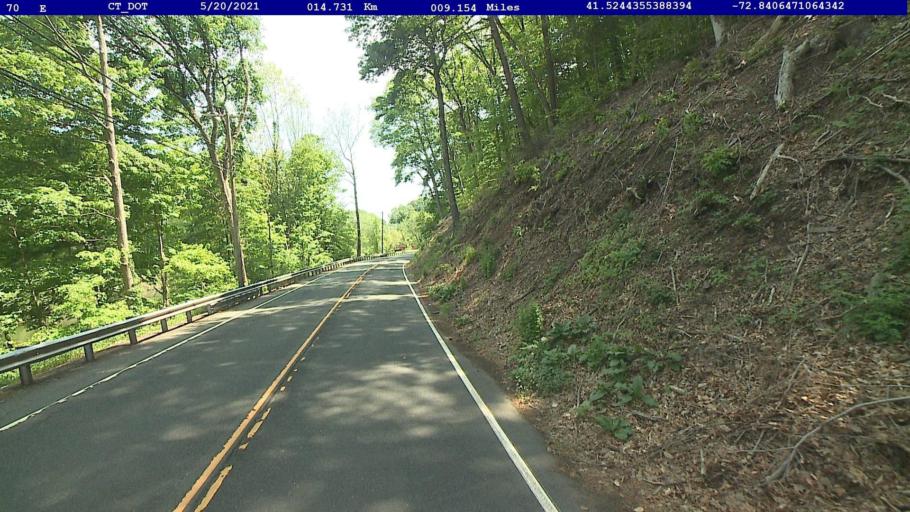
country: US
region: Connecticut
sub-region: New Haven County
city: Meriden
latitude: 41.5241
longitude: -72.8408
